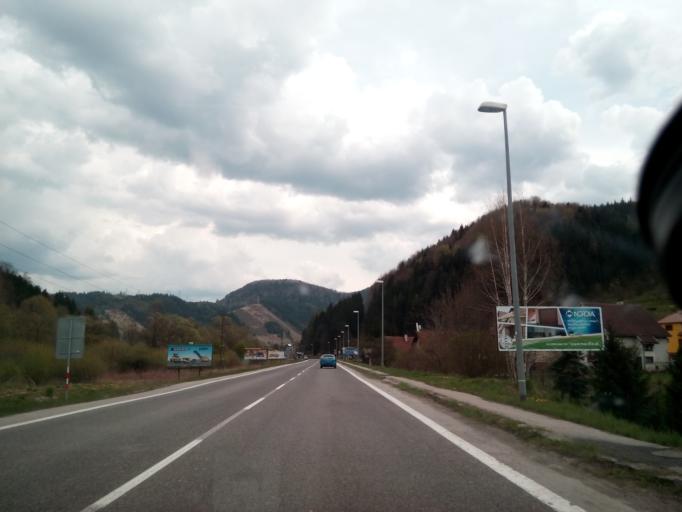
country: SK
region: Zilinsky
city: Ruzomberok
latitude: 49.1215
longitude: 19.1720
